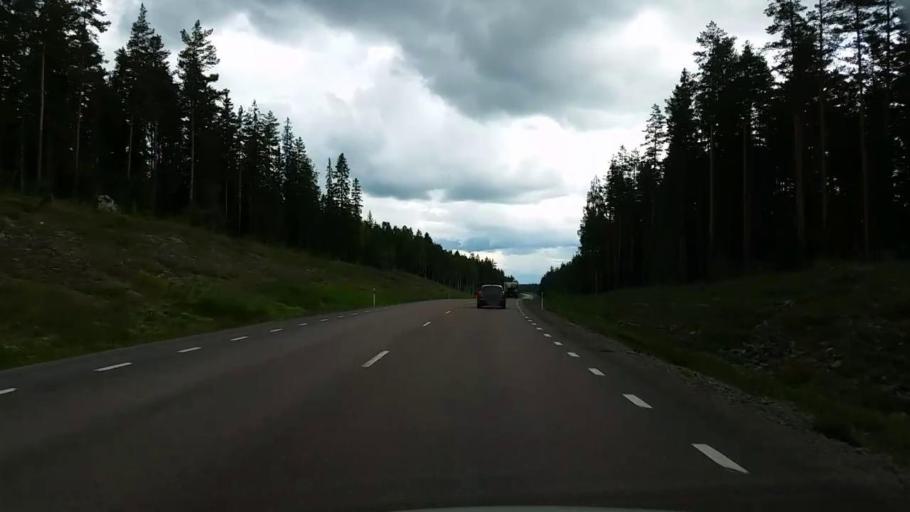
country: SE
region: Dalarna
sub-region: Avesta Kommun
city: Horndal
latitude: 60.4544
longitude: 16.4448
